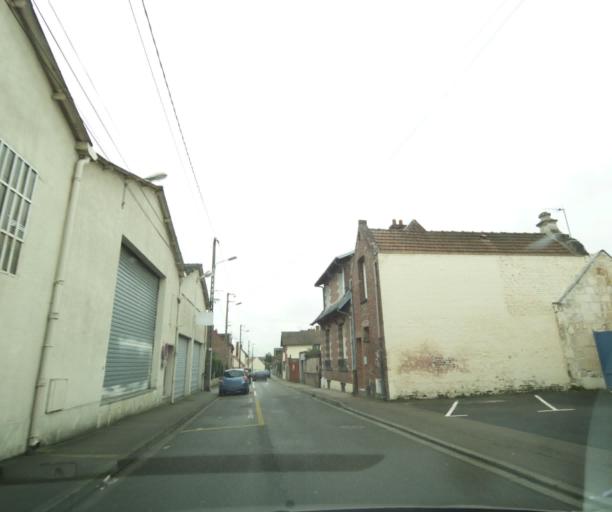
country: FR
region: Picardie
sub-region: Departement de l'Oise
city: Noyon
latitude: 49.5768
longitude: 3.0027
